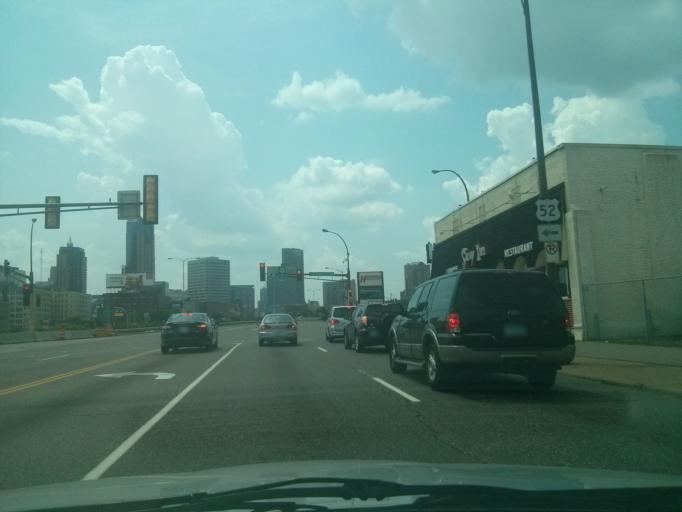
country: US
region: Minnesota
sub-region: Ramsey County
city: Saint Paul
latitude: 44.9536
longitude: -93.0829
